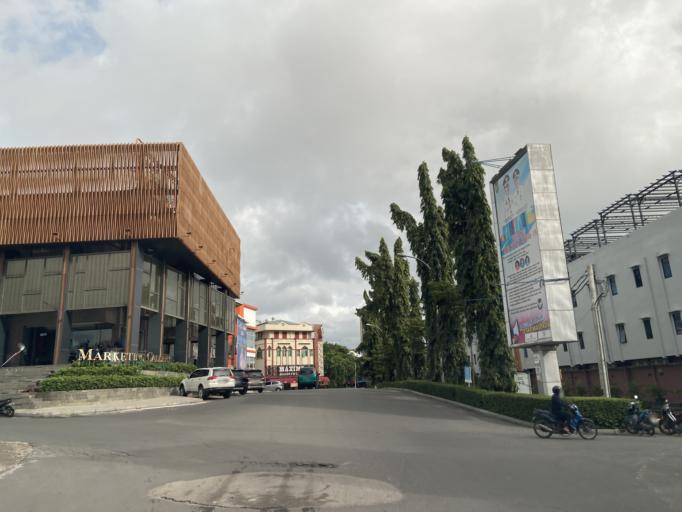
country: SG
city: Singapore
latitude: 1.1444
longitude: 104.0090
